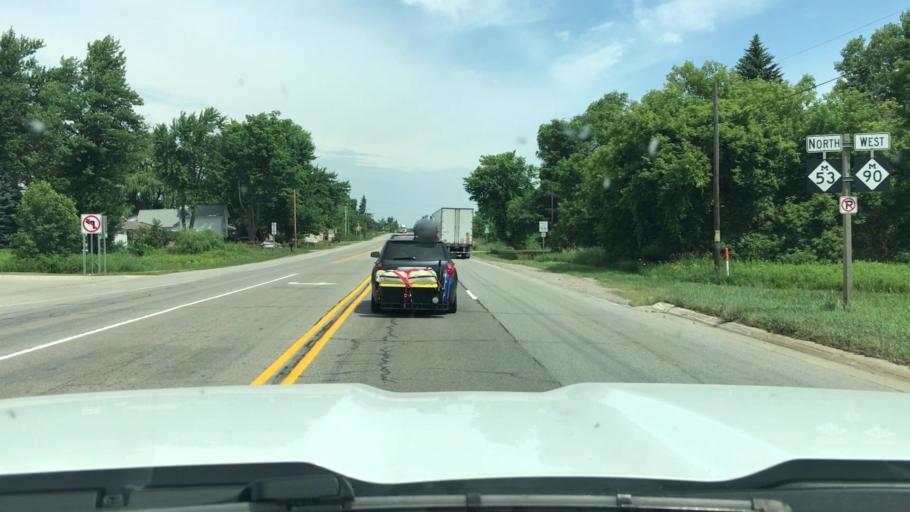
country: US
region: Michigan
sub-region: Sanilac County
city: Brown City
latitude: 43.2109
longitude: -83.0773
